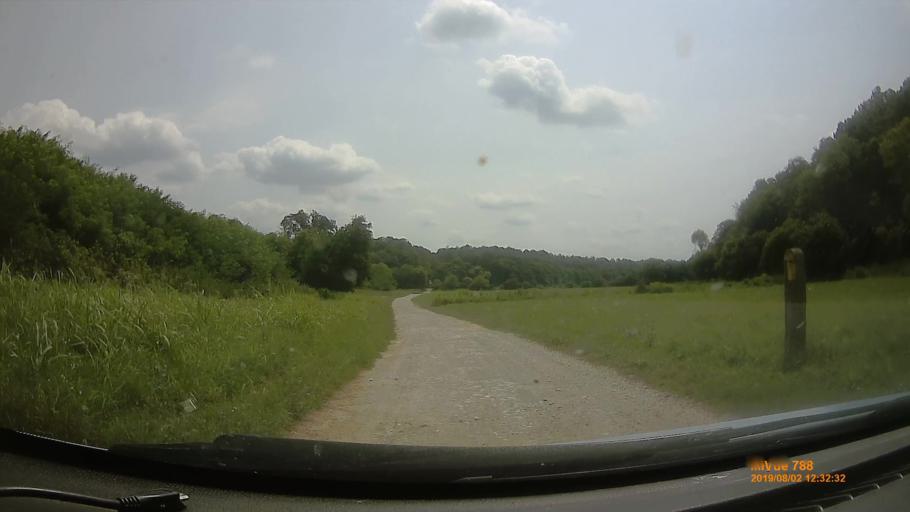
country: HU
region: Baranya
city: Buekkoesd
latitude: 46.1028
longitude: 17.9393
